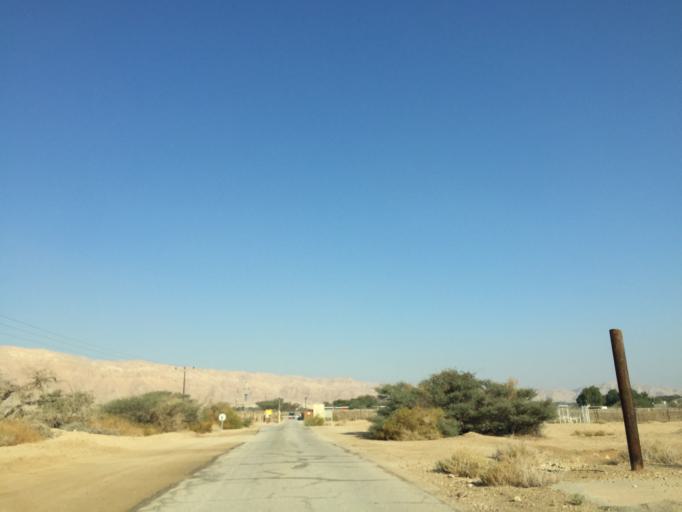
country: JO
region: Ma'an
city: Al Quwayrah
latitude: 29.8445
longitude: 35.0289
